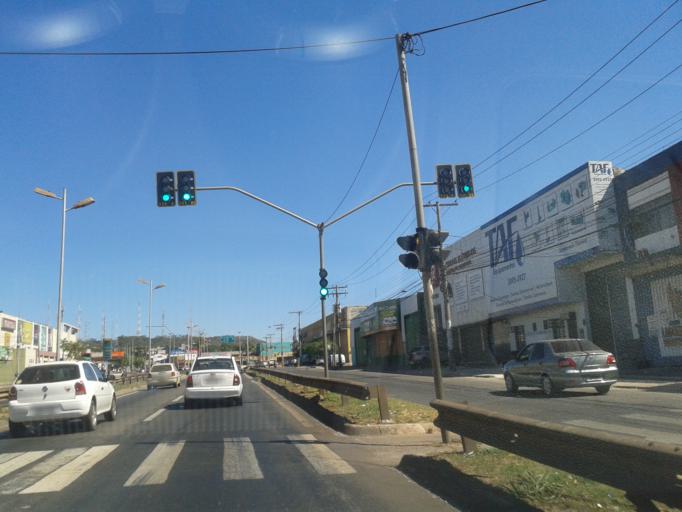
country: BR
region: Goias
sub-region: Goiania
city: Goiania
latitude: -16.6526
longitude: -49.3296
